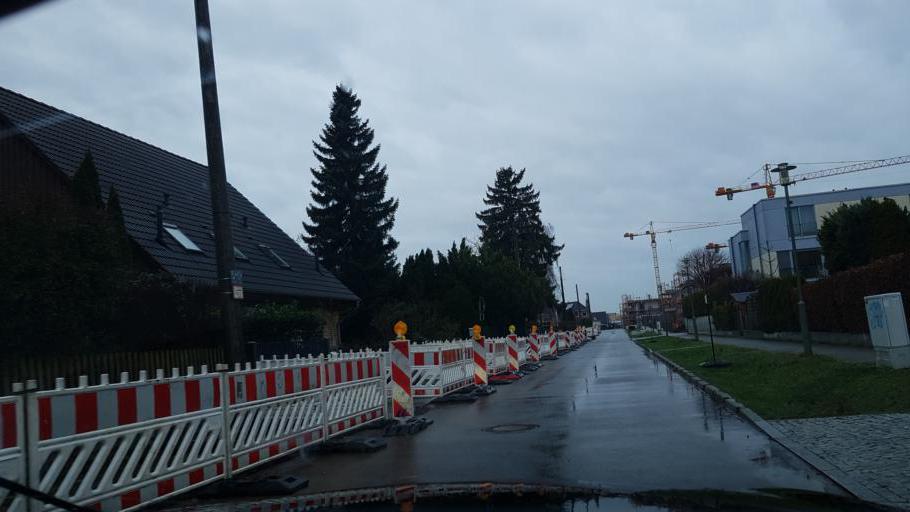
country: DE
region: Berlin
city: Bohnsdorf
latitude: 52.4049
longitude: 13.5664
